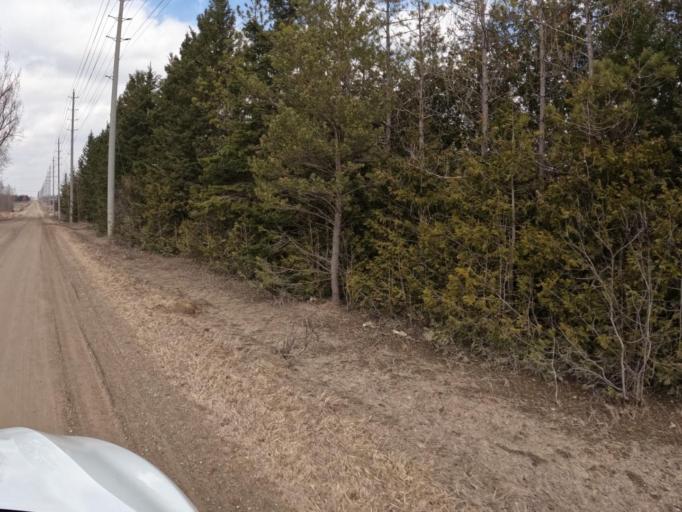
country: CA
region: Ontario
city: Shelburne
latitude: 44.0198
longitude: -80.3127
